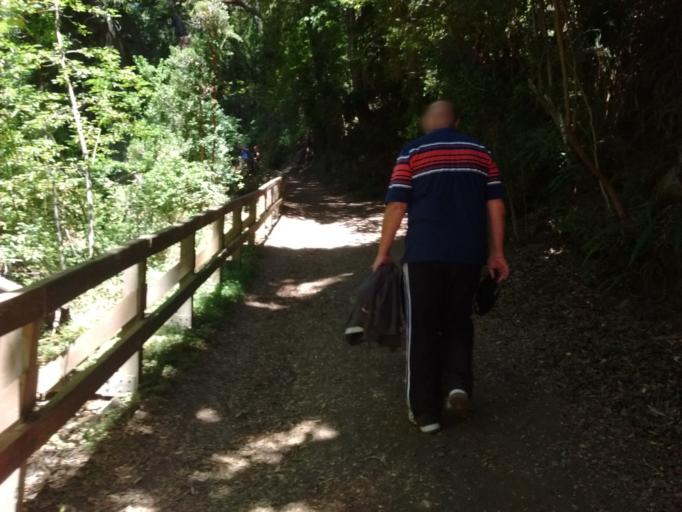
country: AR
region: Neuquen
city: Villa La Angostura
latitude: -40.7848
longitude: -71.6606
